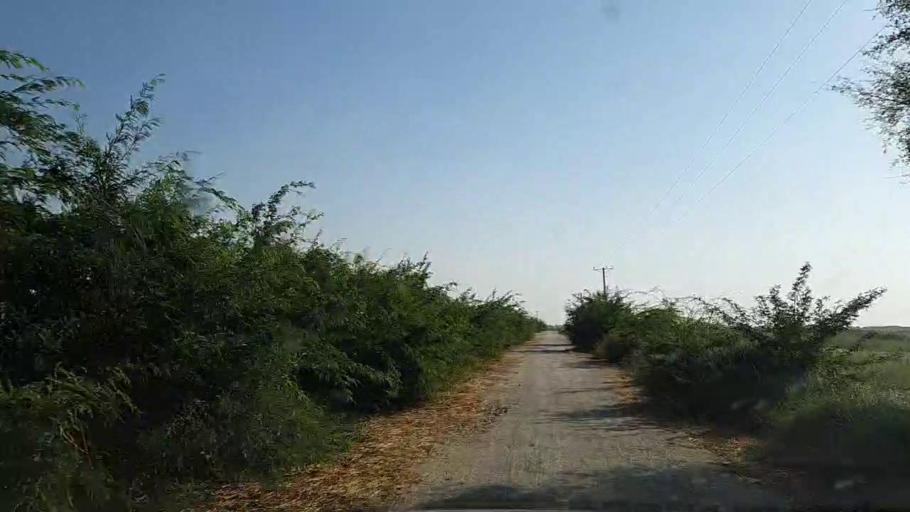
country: PK
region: Sindh
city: Thatta
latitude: 24.6436
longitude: 68.0752
